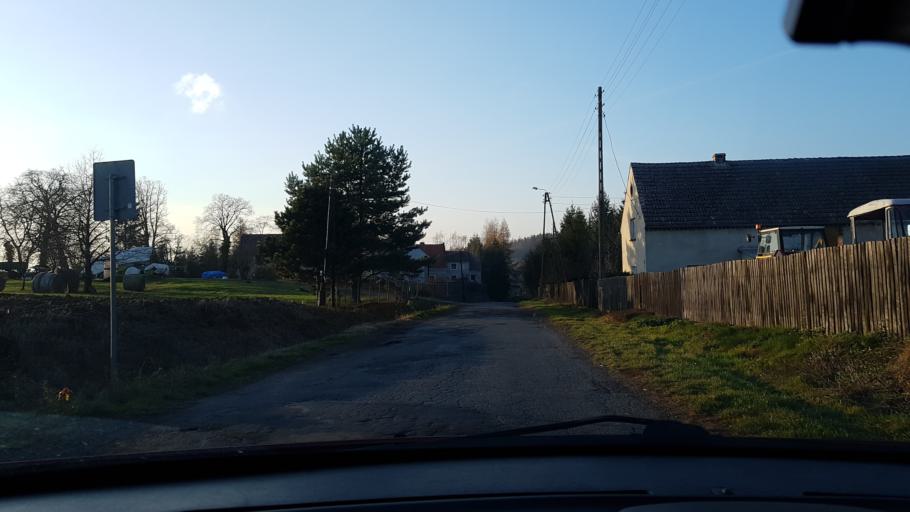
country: PL
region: Lower Silesian Voivodeship
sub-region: Powiat zabkowicki
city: Ziebice
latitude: 50.6576
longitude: 17.0803
